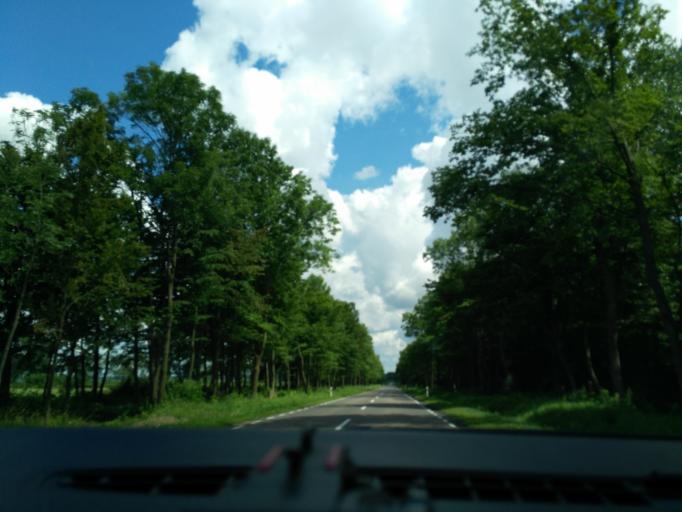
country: PL
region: Podlasie
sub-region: Powiat bielski
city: Bocki
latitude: 52.6180
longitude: 22.9971
